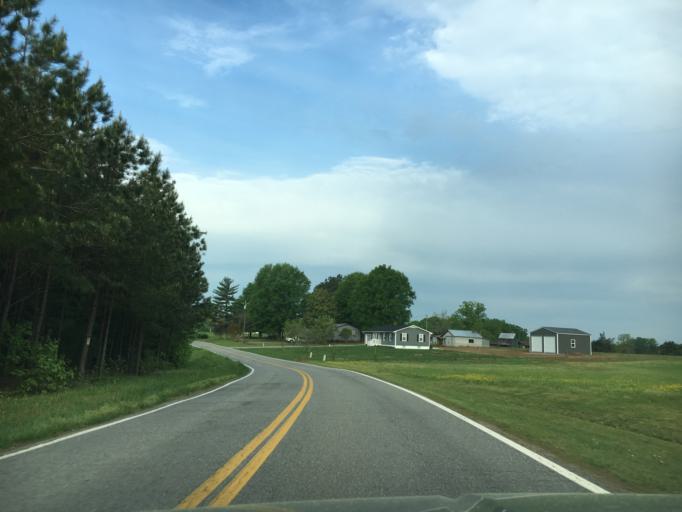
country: US
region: Virginia
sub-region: Halifax County
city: Halifax
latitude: 36.8967
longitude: -78.8244
